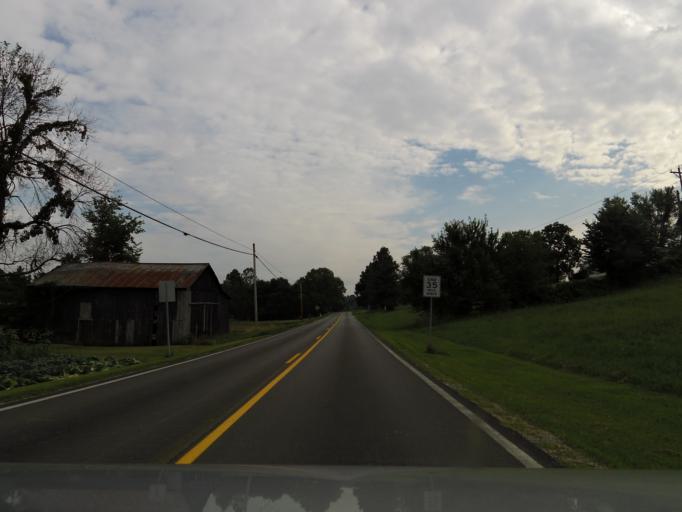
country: US
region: Kentucky
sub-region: Harrison County
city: Cynthiana
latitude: 38.4528
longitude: -84.2401
